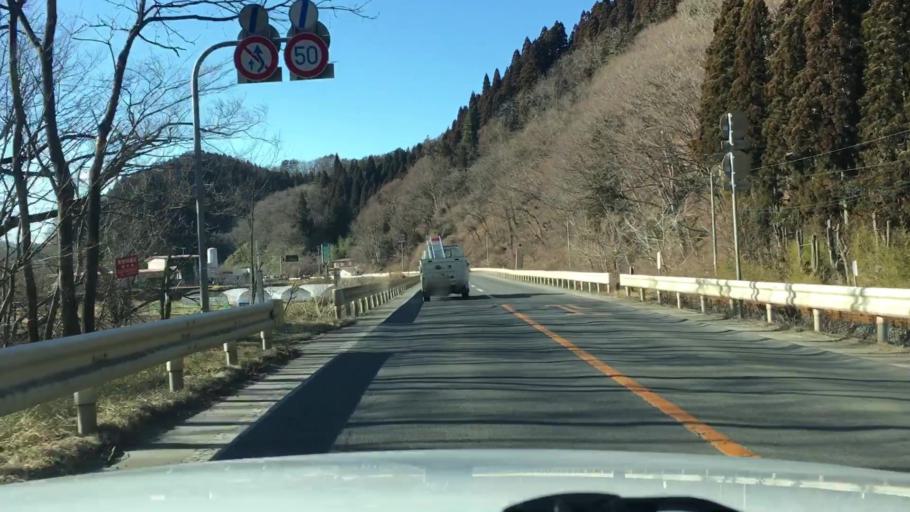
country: JP
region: Iwate
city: Miyako
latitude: 39.6324
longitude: 141.8841
